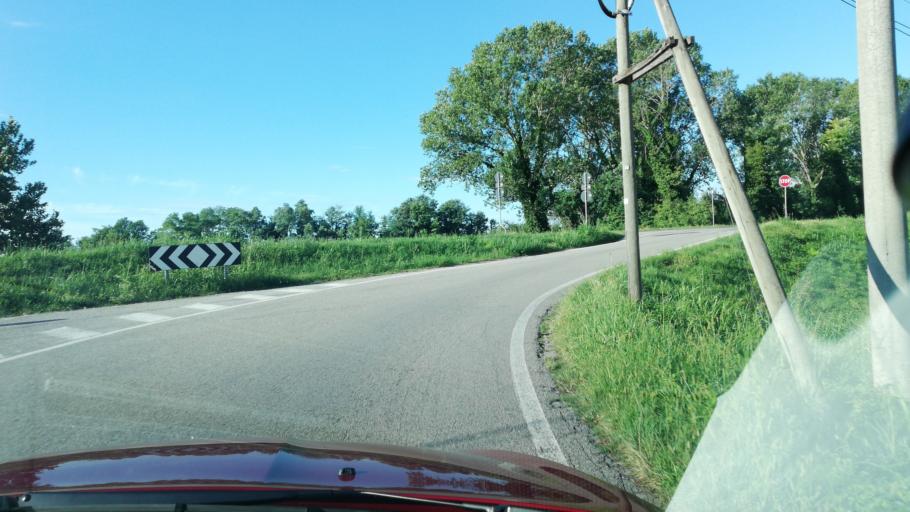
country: IT
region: Veneto
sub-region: Provincia di Venezia
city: Eraclea
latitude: 45.5760
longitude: 12.6854
